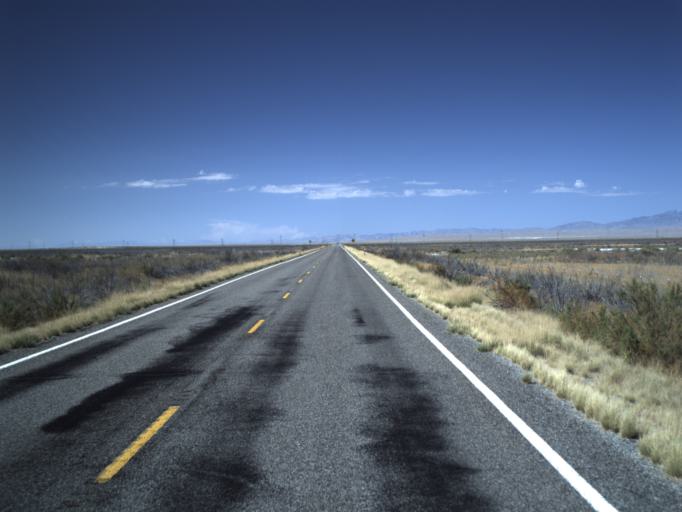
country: US
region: Utah
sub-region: Millard County
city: Delta
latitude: 39.2681
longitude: -112.8669
